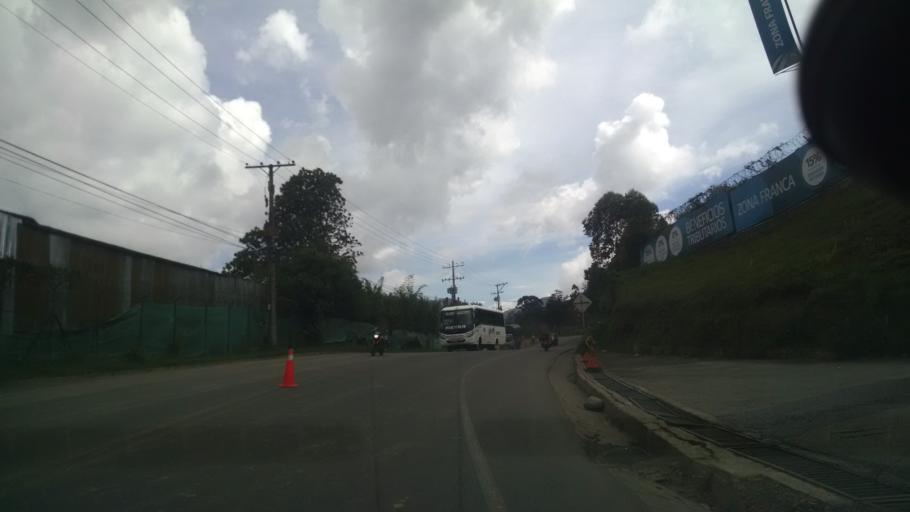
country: CO
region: Antioquia
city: Caldas
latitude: 6.0667
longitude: -75.6337
